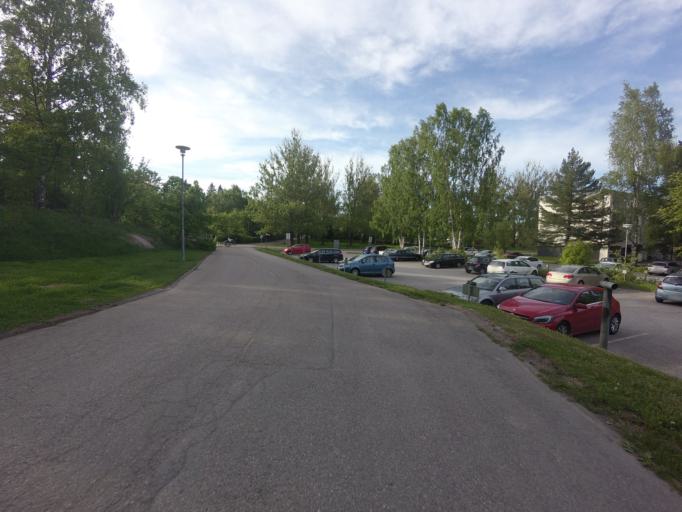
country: FI
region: Uusimaa
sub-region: Helsinki
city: Koukkuniemi
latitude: 60.1570
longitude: 24.7487
